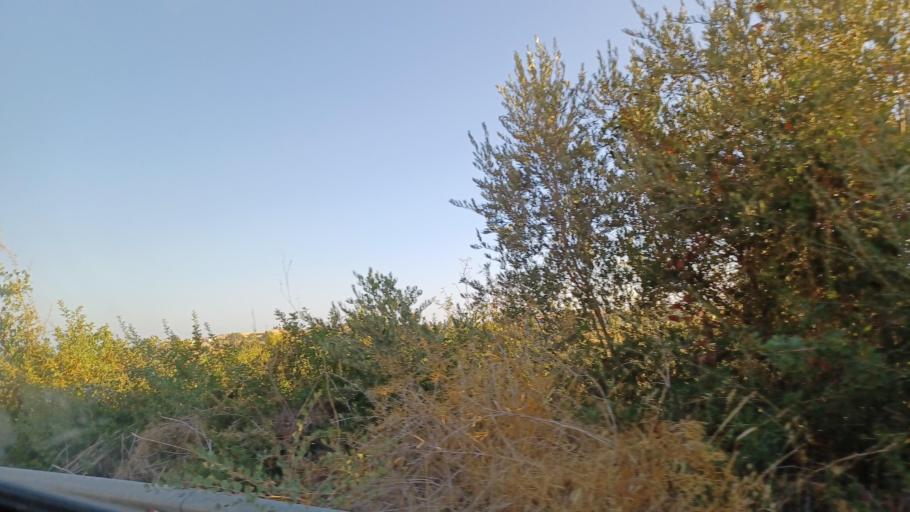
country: CY
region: Pafos
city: Polis
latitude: 34.9960
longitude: 32.4386
